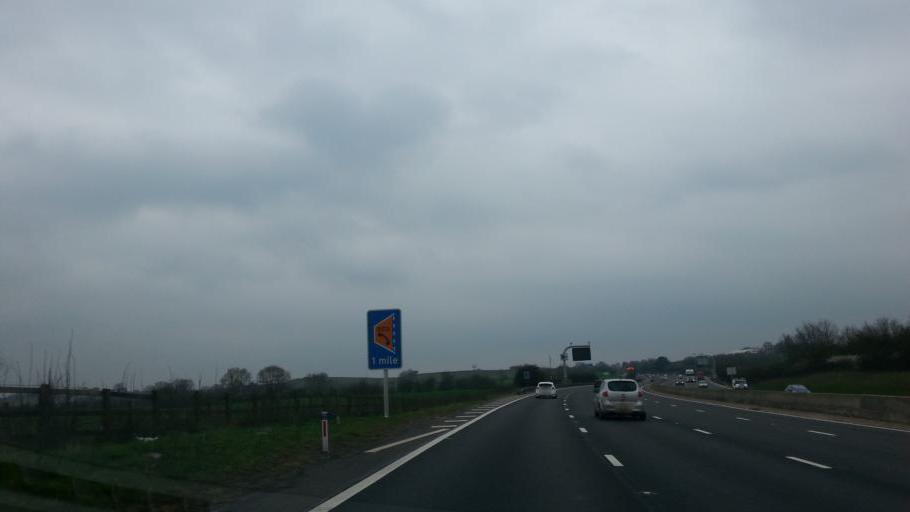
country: GB
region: England
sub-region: Worcestershire
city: Bromsgrove
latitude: 52.3224
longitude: -2.0936
